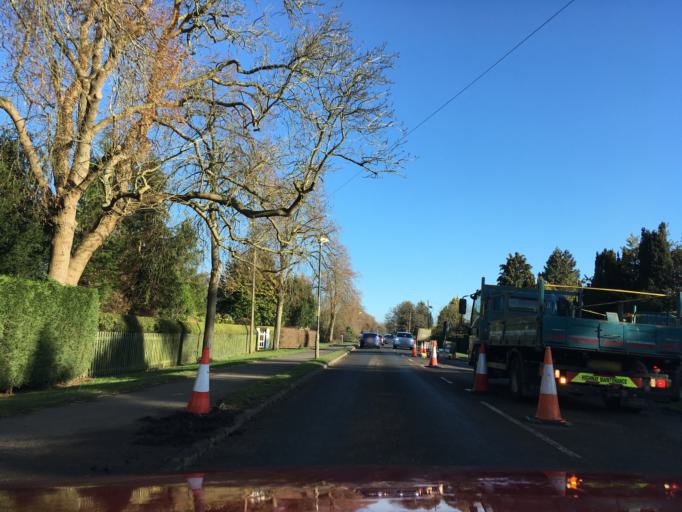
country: GB
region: England
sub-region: Warwickshire
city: Stratford-upon-Avon
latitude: 52.1962
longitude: -1.6886
